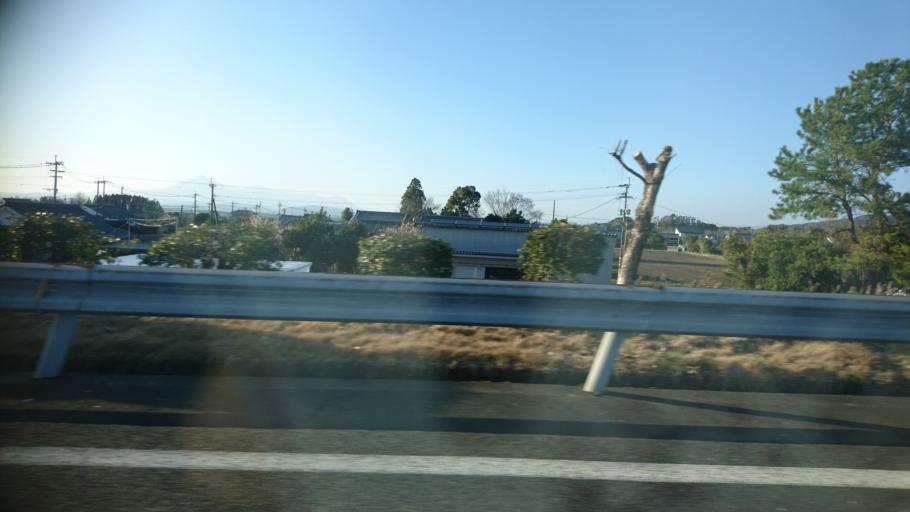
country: JP
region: Miyazaki
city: Miyakonojo
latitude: 31.7880
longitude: 131.1501
